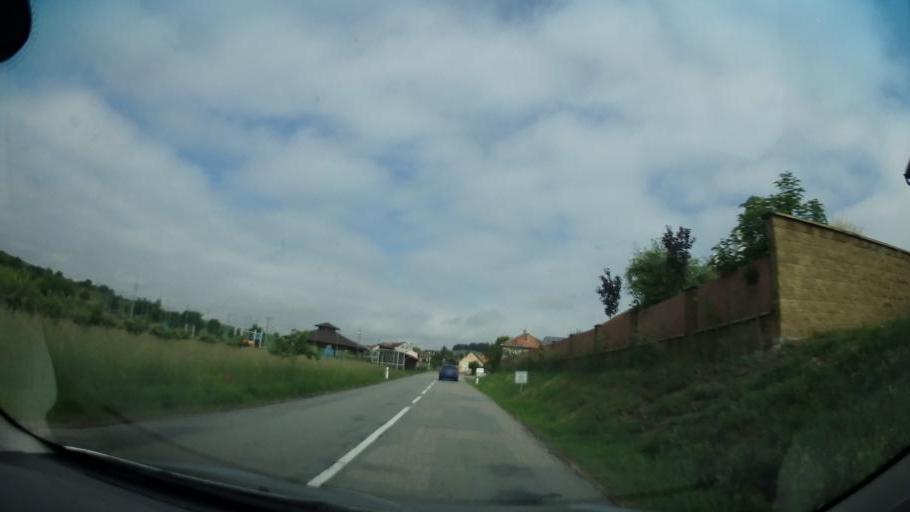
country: CZ
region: South Moravian
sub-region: Okres Brno-Venkov
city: Dolni Loucky
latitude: 49.3773
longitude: 16.3539
